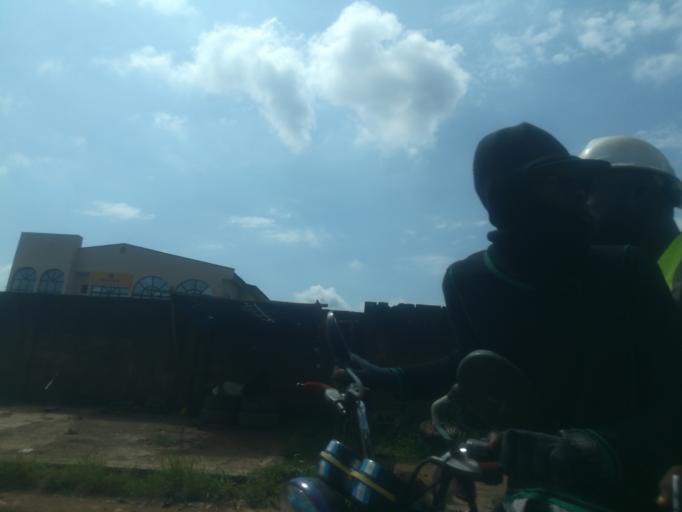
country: NG
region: Oyo
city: Ibadan
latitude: 7.4222
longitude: 3.9779
